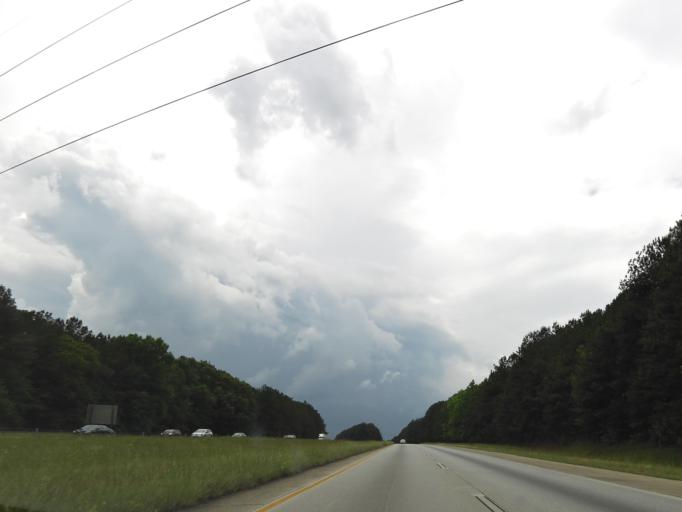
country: US
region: Georgia
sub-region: Carroll County
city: Temple
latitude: 33.7079
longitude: -85.0513
